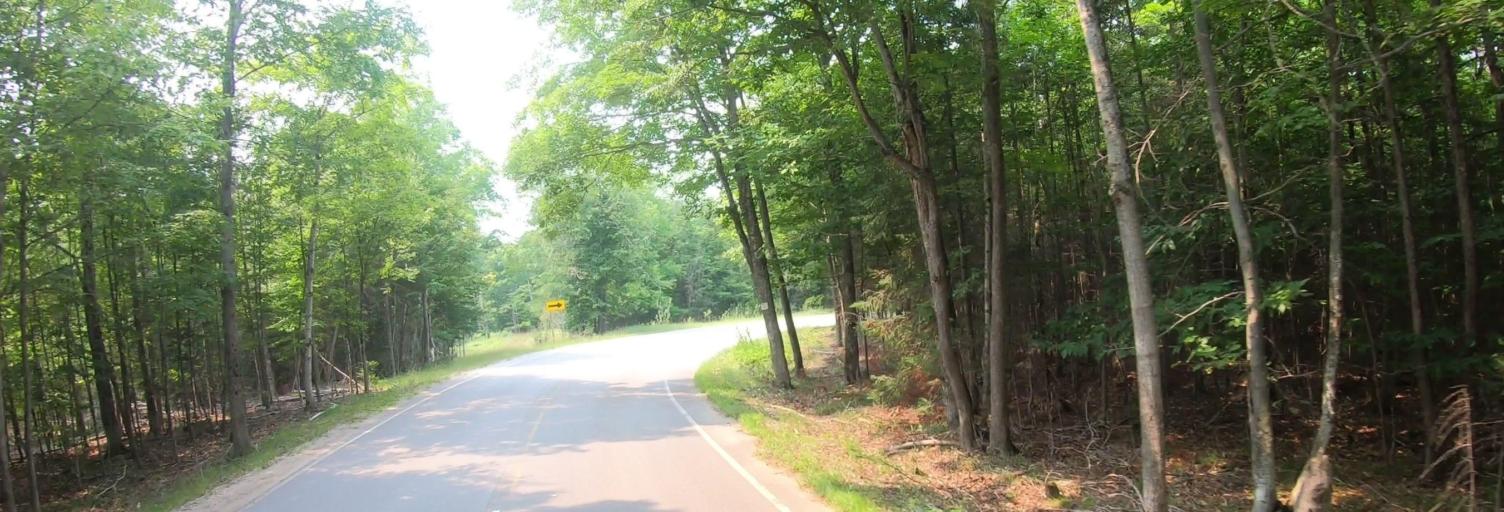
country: CA
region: Ontario
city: Thessalon
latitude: 46.0125
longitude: -83.7060
